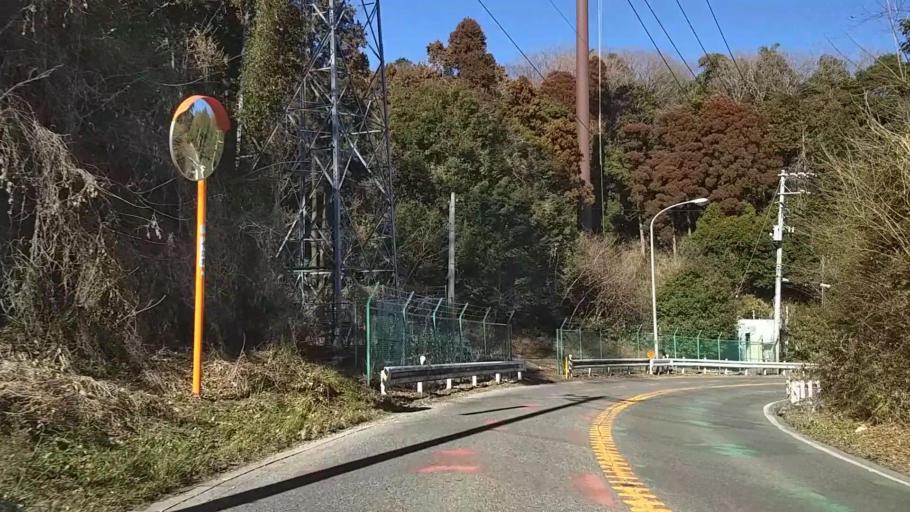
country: JP
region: Kanagawa
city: Zushi
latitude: 35.3313
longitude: 139.5902
